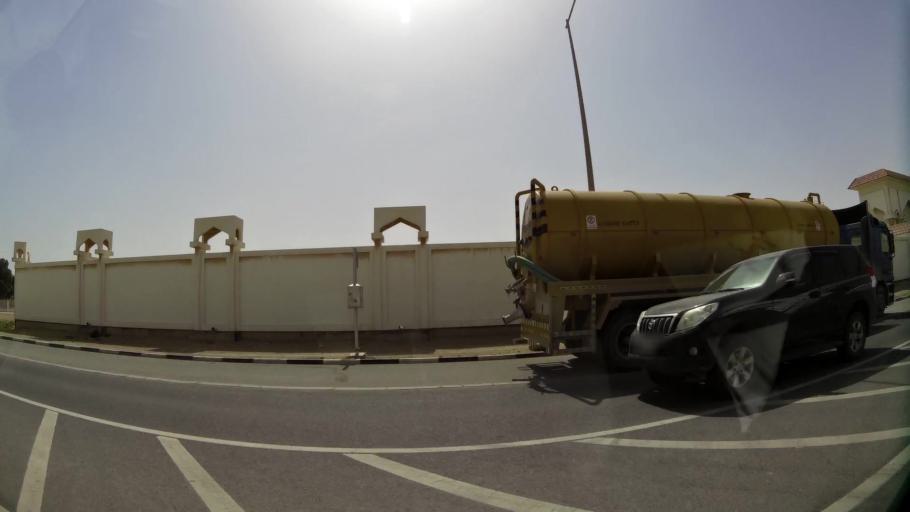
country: QA
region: Baladiyat Umm Salal
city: Umm Salal Muhammad
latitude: 25.4051
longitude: 51.4180
